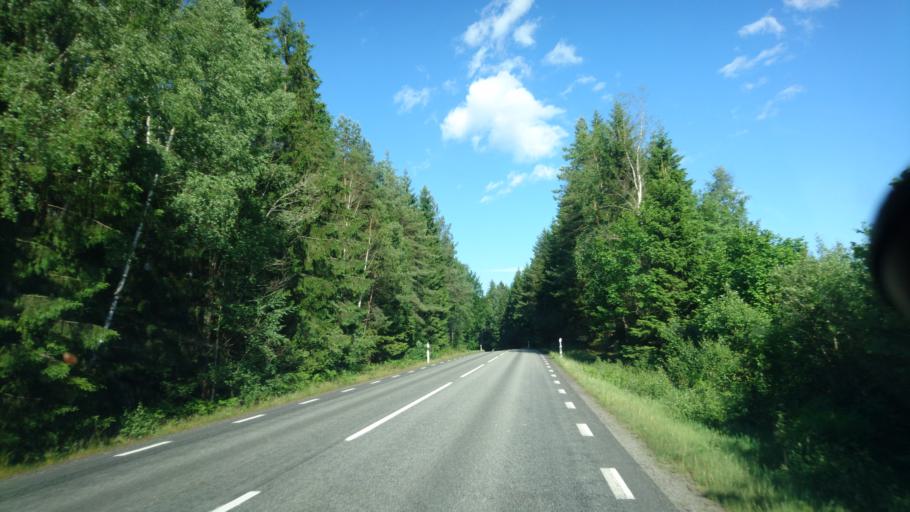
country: SE
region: Skane
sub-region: Osby Kommun
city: Lonsboda
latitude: 56.3893
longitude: 14.4132
